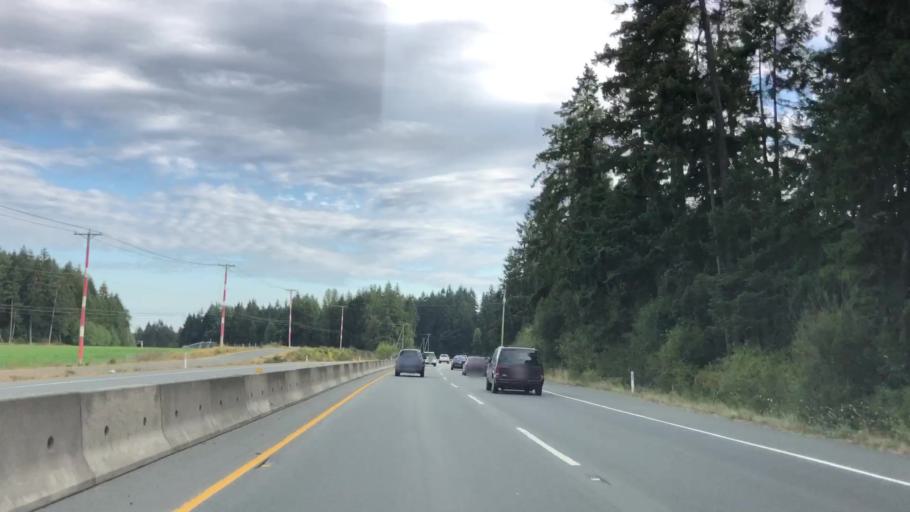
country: CA
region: British Columbia
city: Duncan
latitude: 48.7251
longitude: -123.6363
